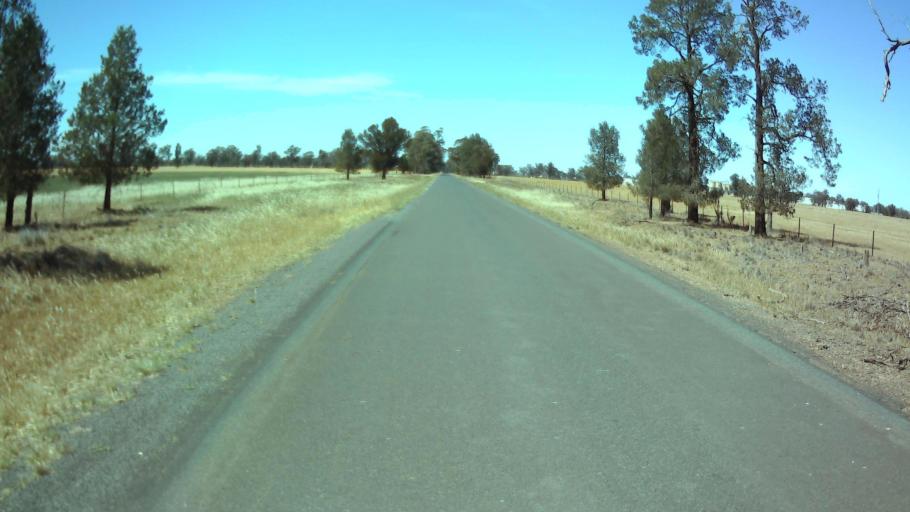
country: AU
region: New South Wales
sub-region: Weddin
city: Grenfell
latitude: -34.1059
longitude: 147.8867
